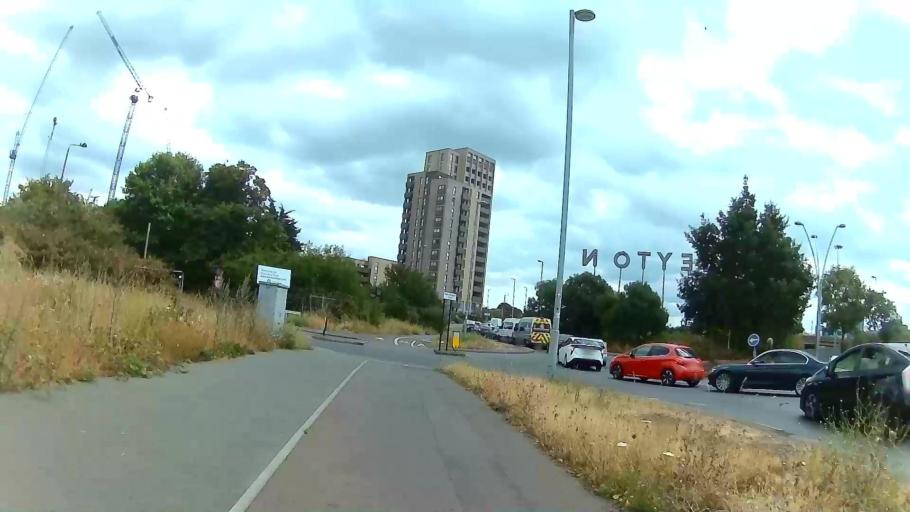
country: GB
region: England
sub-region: Greater London
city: Walthamstow
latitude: 51.5578
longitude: -0.0164
